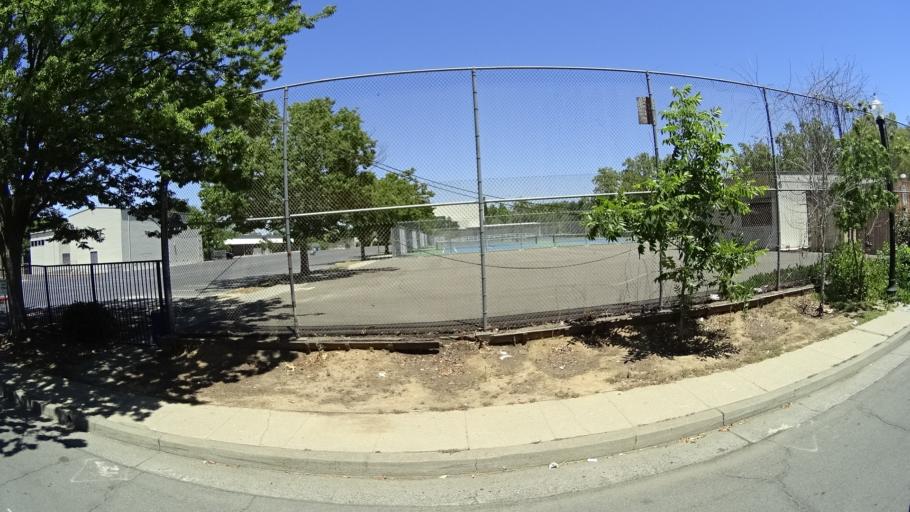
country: US
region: California
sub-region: Sacramento County
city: Sacramento
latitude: 38.5543
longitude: -121.4656
